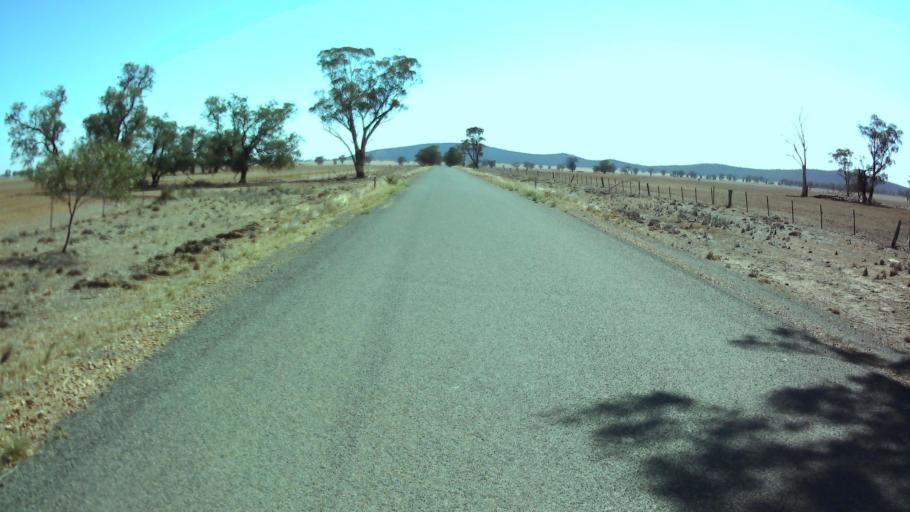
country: AU
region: New South Wales
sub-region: Weddin
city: Grenfell
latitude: -33.7137
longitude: 147.9082
